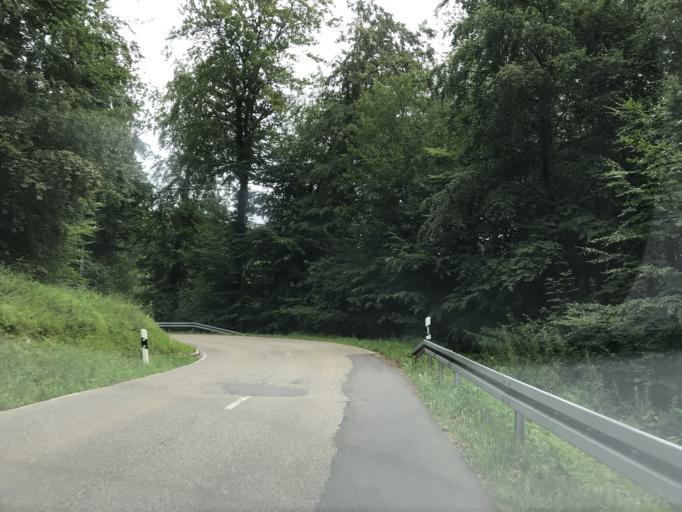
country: DE
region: Baden-Wuerttemberg
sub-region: Freiburg Region
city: Hasel
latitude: 47.6664
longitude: 7.8794
